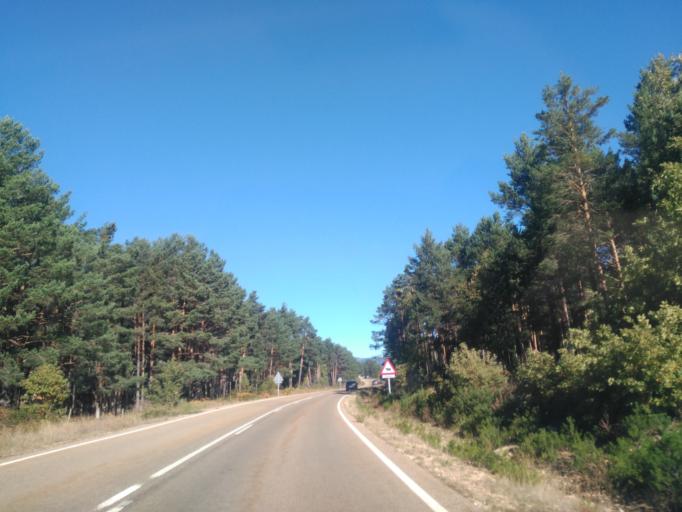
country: ES
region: Castille and Leon
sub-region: Provincia de Soria
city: Vinuesa
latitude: 41.9312
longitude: -2.7653
